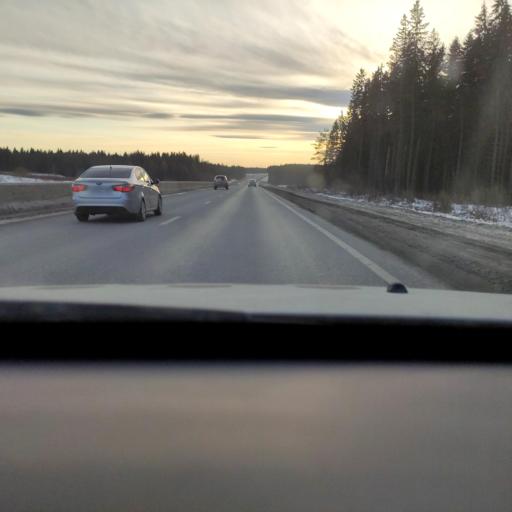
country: RU
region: Perm
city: Ferma
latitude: 57.9636
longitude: 56.3986
